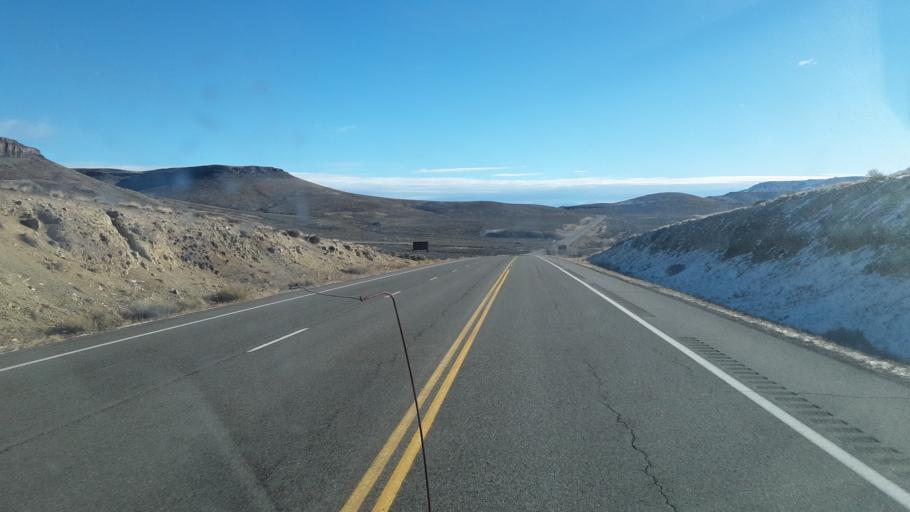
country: US
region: Colorado
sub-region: Gunnison County
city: Gunnison
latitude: 38.4721
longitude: -107.1513
